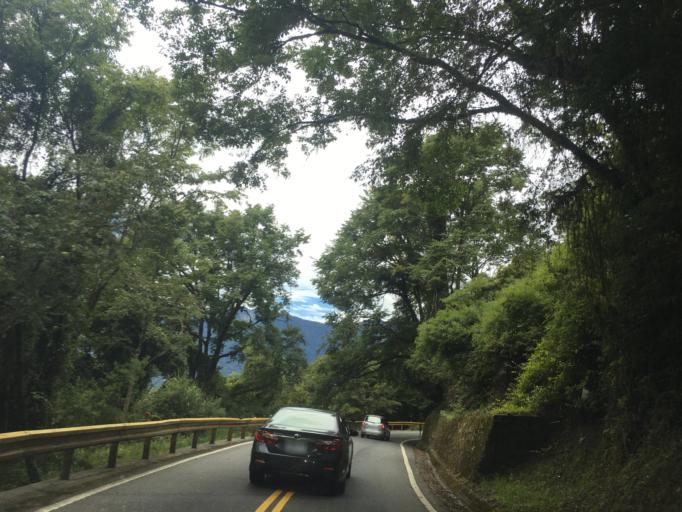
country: TW
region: Taiwan
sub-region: Hualien
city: Hualian
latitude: 24.1759
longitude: 121.3817
